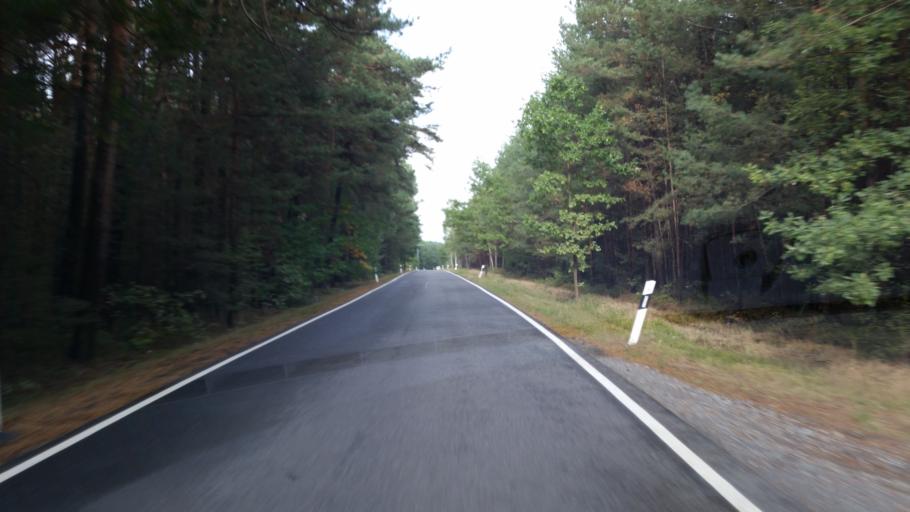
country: DE
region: Brandenburg
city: Grunewald
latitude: 51.3746
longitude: 13.9761
